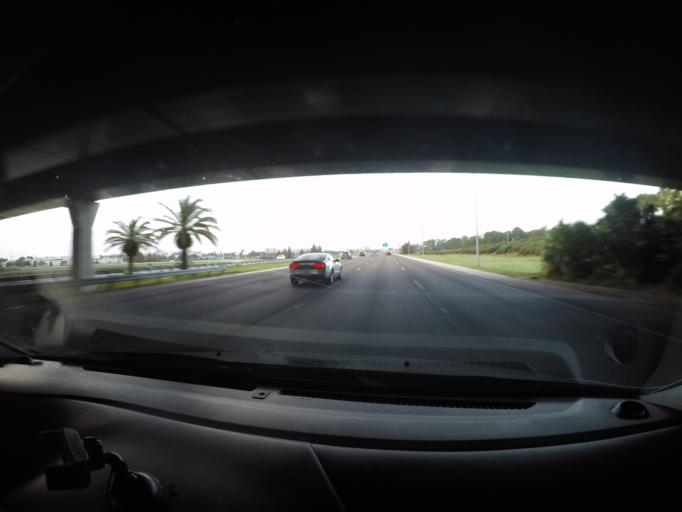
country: US
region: Florida
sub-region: Orange County
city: Oak Ridge
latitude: 28.4934
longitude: -81.4336
